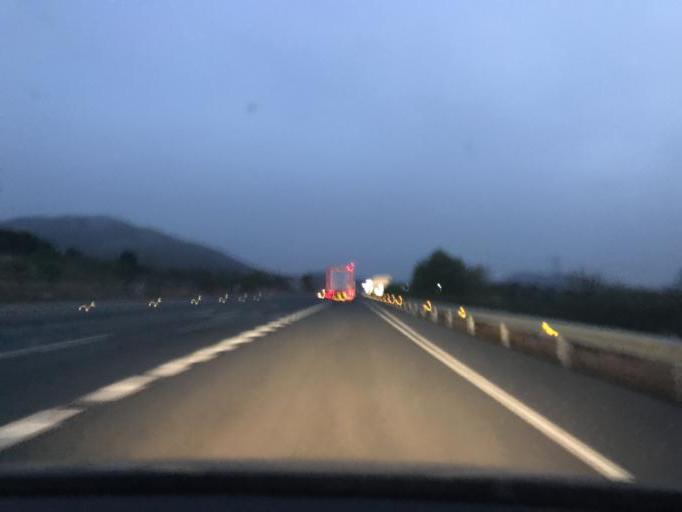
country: ES
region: Andalusia
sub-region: Provincia de Granada
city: Gor
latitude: 37.4186
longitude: -2.9178
